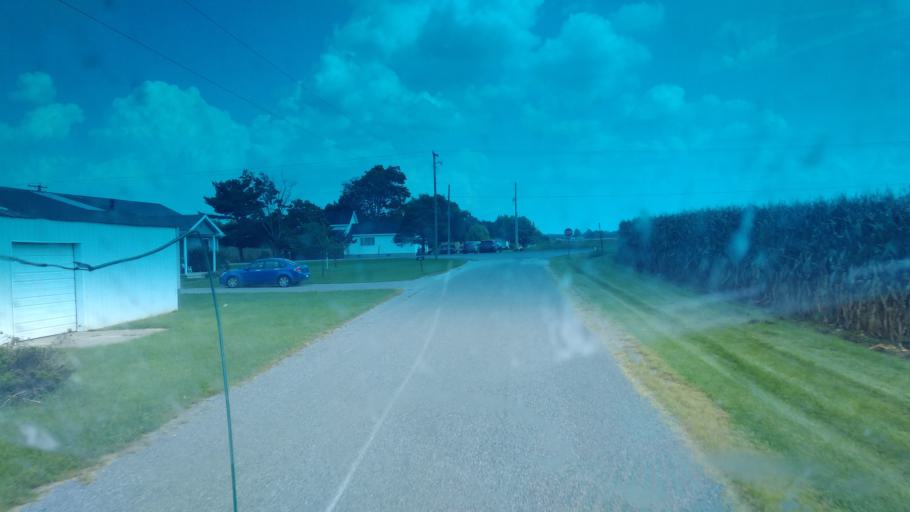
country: US
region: Ohio
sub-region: Hardin County
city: Ada
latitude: 40.7185
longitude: -83.7861
